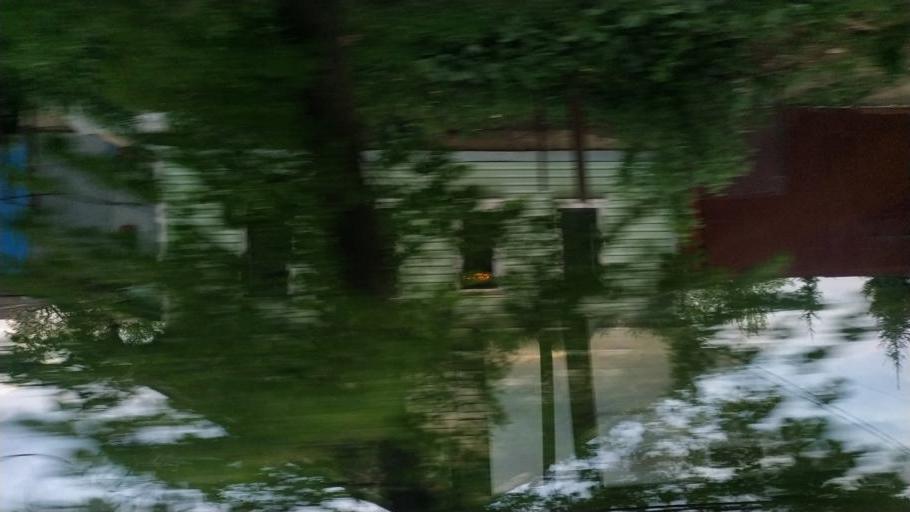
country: RU
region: Moskovskaya
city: Kashira
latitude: 54.8400
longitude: 38.1647
